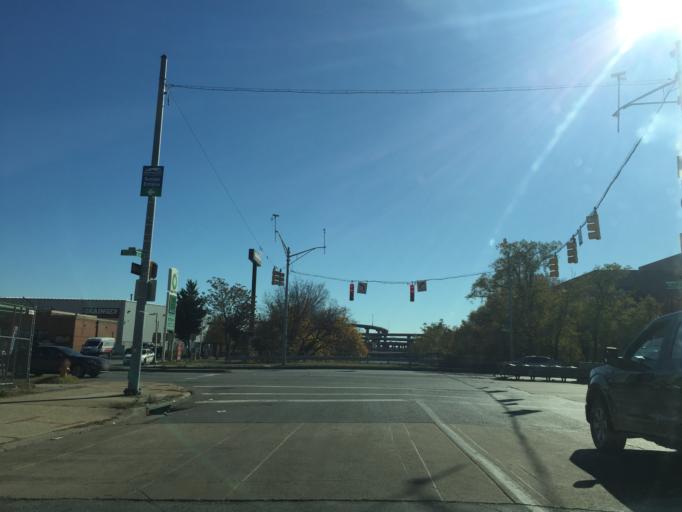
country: US
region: Maryland
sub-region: City of Baltimore
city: Baltimore
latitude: 39.2726
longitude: -76.6303
